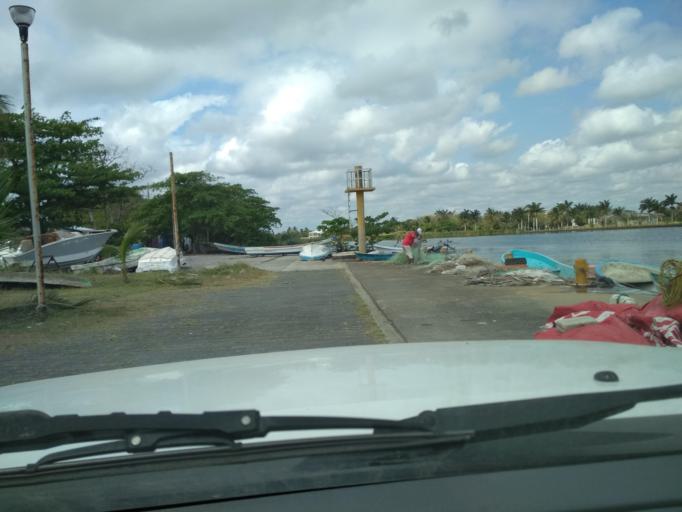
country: MX
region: Veracruz
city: Boca del Rio
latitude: 19.0979
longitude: -96.1083
